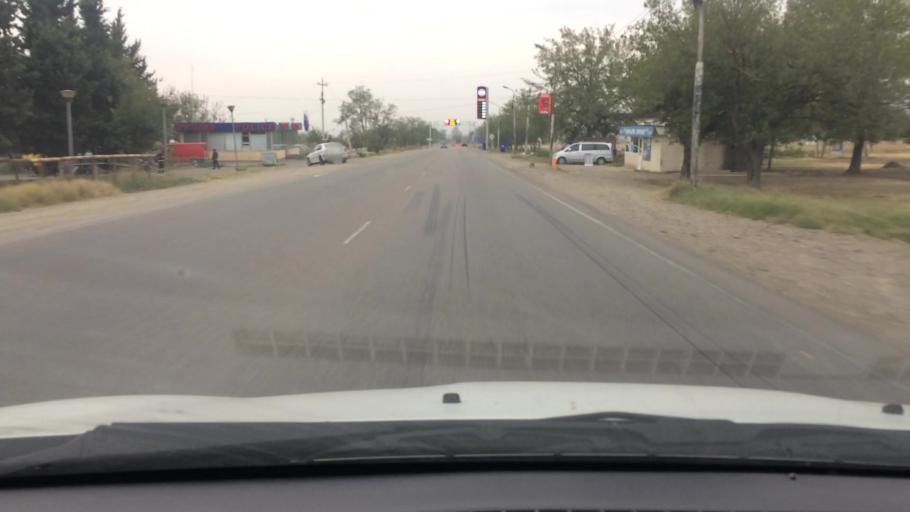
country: GE
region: Kvemo Kartli
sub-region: Marneuli
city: Marneuli
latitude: 41.5752
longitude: 44.7748
